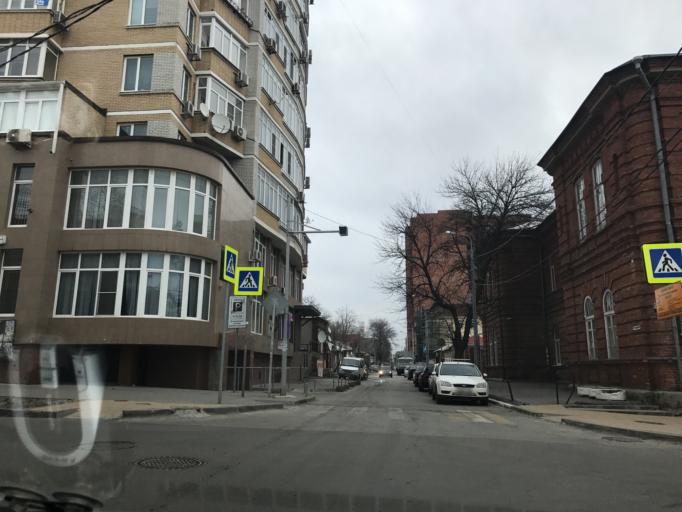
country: RU
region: Rostov
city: Rostov-na-Donu
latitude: 47.2236
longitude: 39.7350
